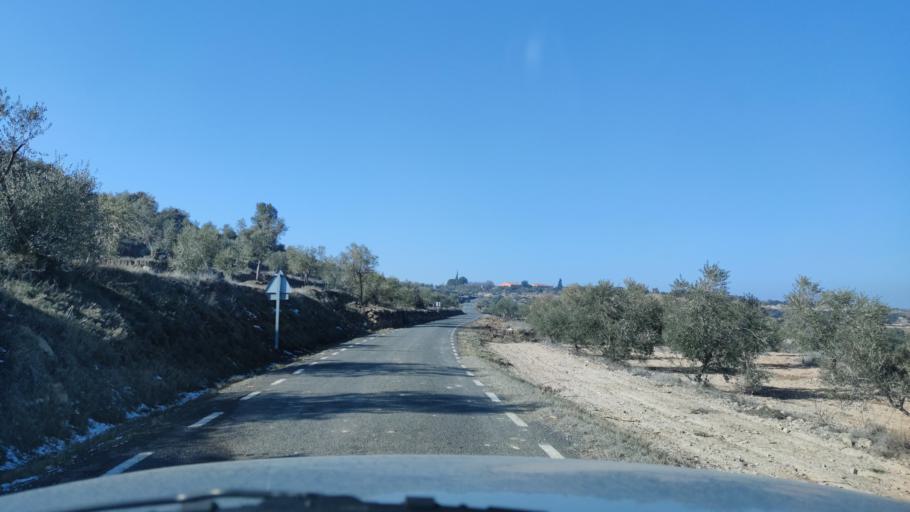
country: ES
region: Catalonia
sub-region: Provincia de Lleida
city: Torrebesses
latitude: 41.4343
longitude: 0.5728
